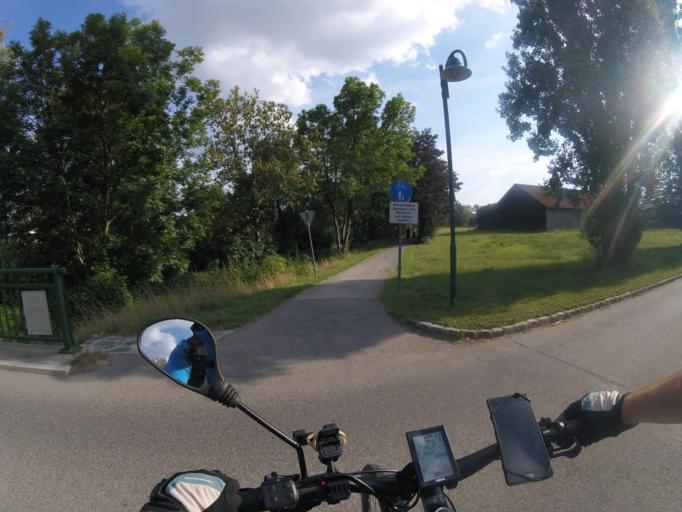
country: AT
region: Lower Austria
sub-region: Politischer Bezirk Baden
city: Trumau
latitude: 47.9925
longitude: 16.3481
